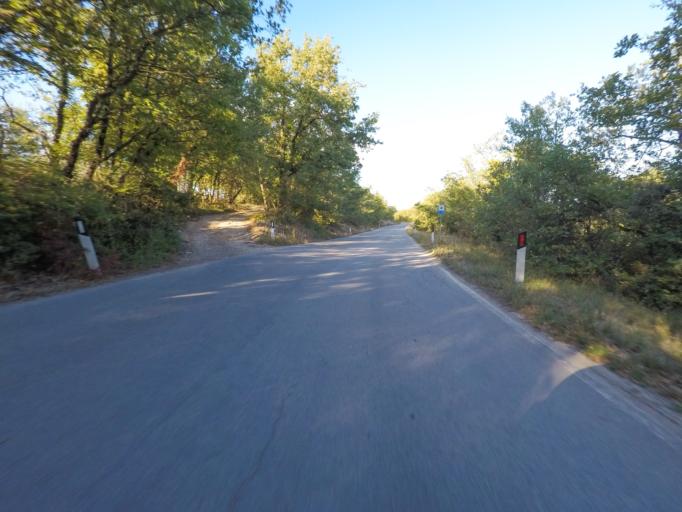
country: IT
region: Tuscany
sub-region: Provincia di Siena
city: Radda in Chianti
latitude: 43.4440
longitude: 11.3938
